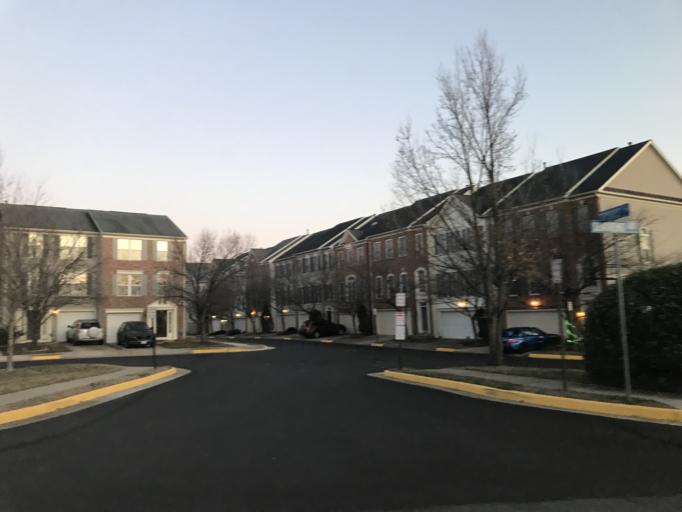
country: US
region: Virginia
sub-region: Fairfax County
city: Franconia
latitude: 38.7755
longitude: -77.1600
